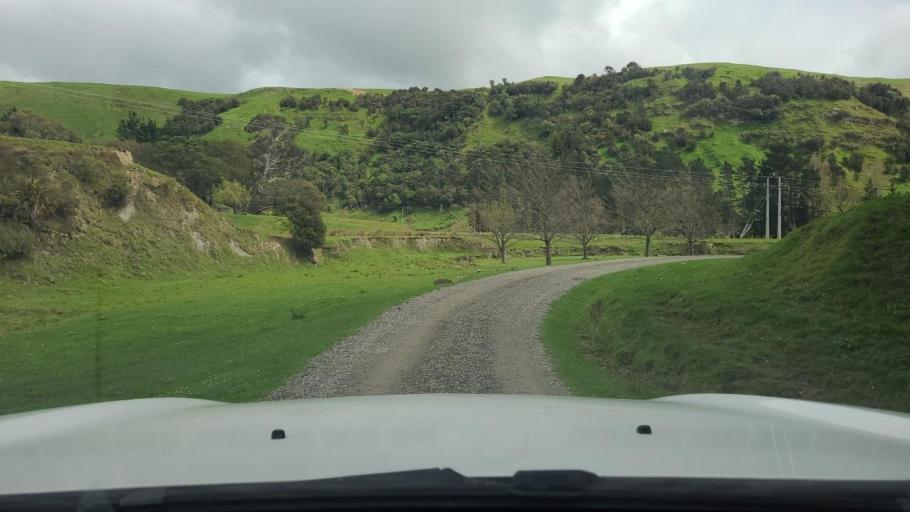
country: NZ
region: Wellington
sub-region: South Wairarapa District
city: Waipawa
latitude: -41.3171
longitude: 175.4727
